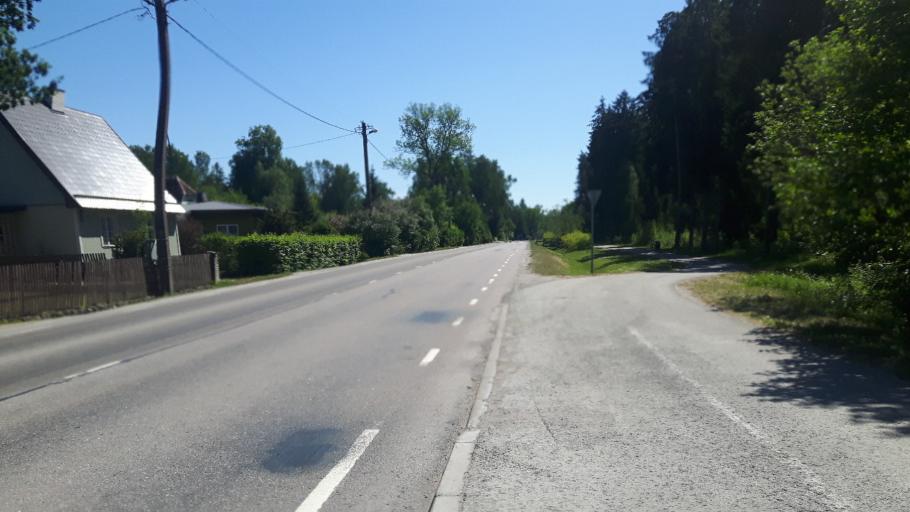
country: EE
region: Harju
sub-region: Saku vald
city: Saku
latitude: 59.2385
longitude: 24.6812
